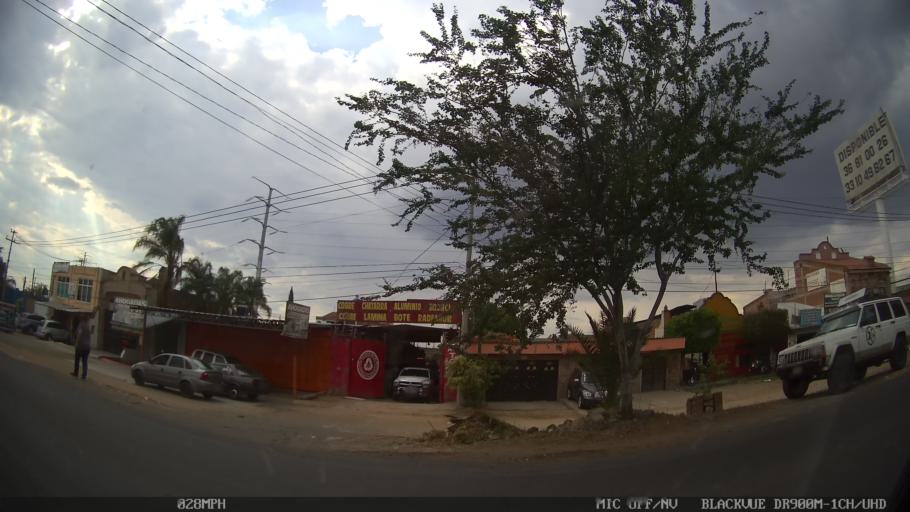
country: MX
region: Jalisco
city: Tonala
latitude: 20.6175
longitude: -103.2664
